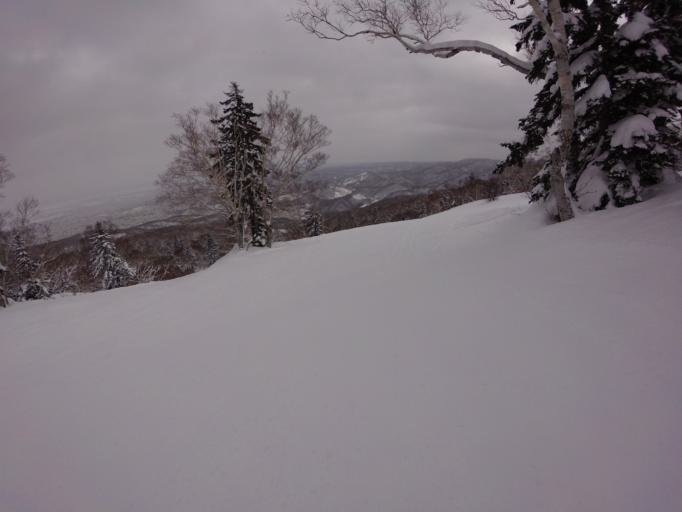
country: JP
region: Hokkaido
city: Sapporo
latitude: 43.0725
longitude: 141.2026
